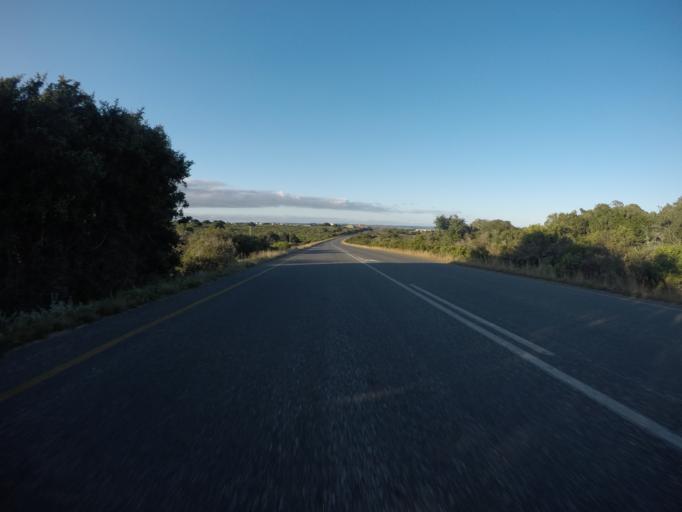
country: ZA
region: Western Cape
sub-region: Eden District Municipality
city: Riversdale
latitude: -34.3902
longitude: 21.3973
